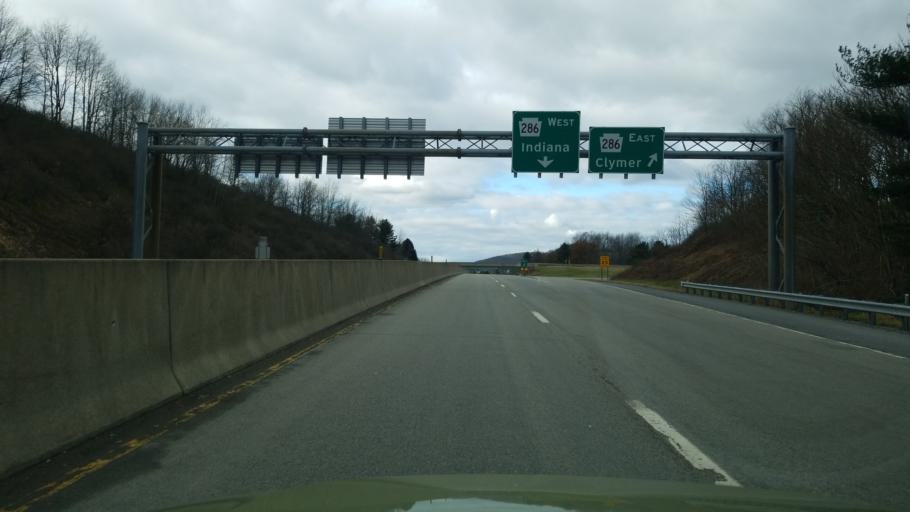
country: US
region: Pennsylvania
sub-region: Indiana County
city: Chevy Chase Heights
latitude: 40.6265
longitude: -79.1225
